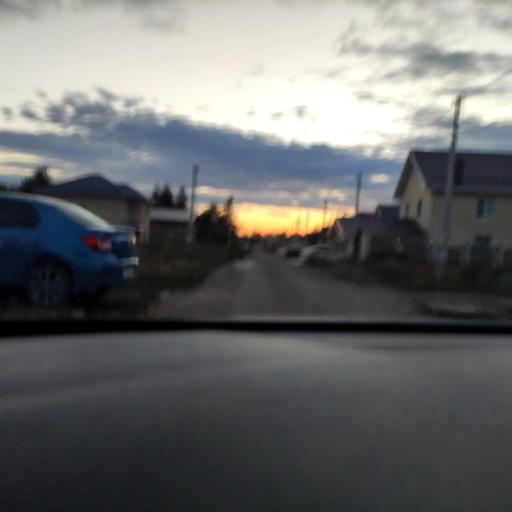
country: RU
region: Tatarstan
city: Stolbishchi
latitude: 55.7223
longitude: 49.3054
